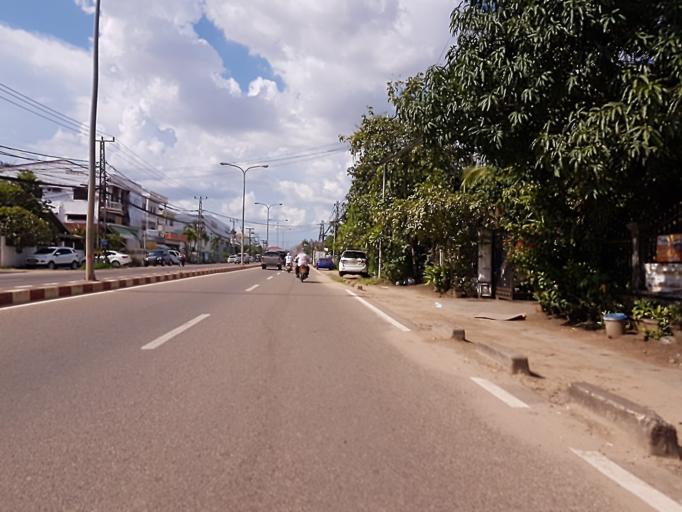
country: TH
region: Nong Khai
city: Si Chiang Mai
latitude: 17.9151
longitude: 102.6200
